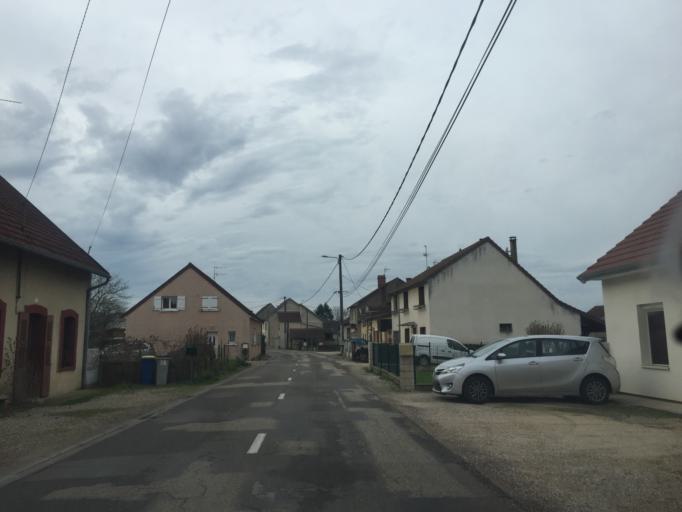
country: FR
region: Franche-Comte
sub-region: Departement du Jura
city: Choisey
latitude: 47.0417
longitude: 5.4444
